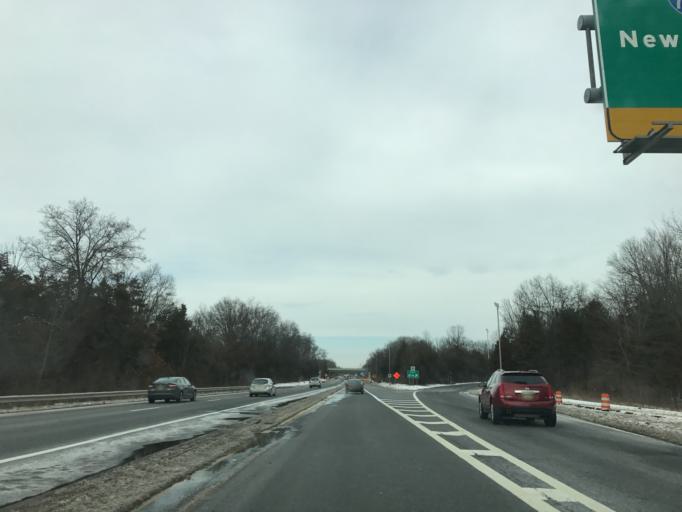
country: US
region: New Jersey
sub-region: Somerset County
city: Bridgewater
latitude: 40.6382
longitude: -74.6442
